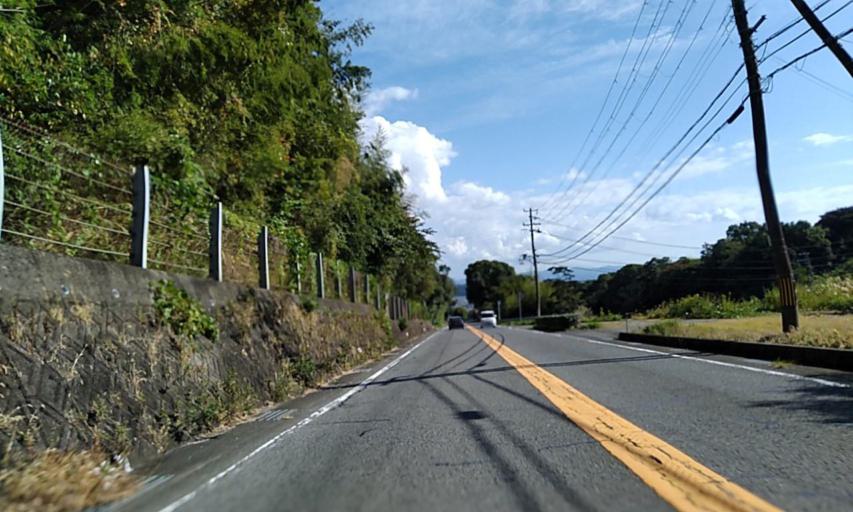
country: JP
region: Wakayama
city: Tanabe
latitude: 33.7807
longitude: 135.3040
